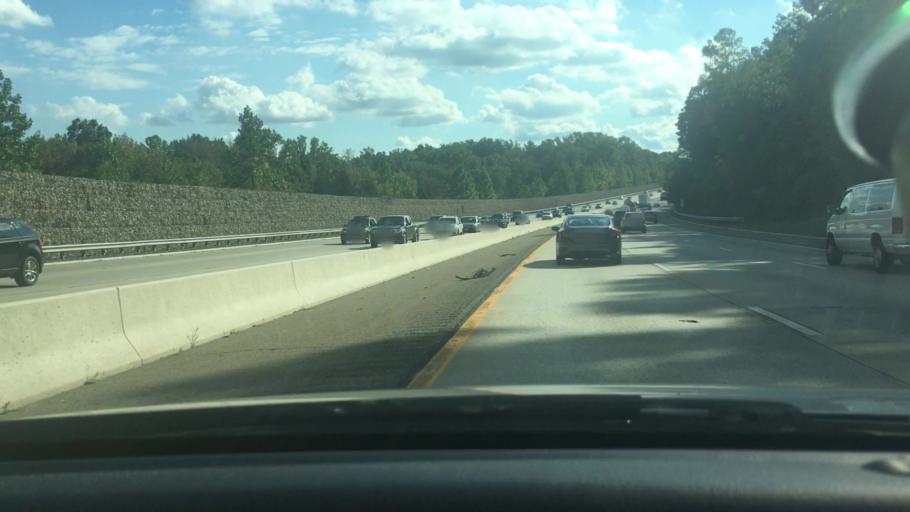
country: US
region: New Jersey
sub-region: Morris County
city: Lincoln Park
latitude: 40.9391
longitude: -74.3493
